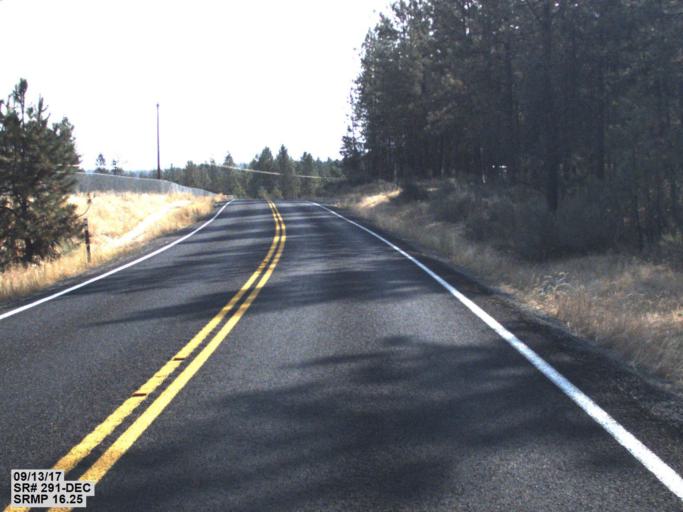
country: US
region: Washington
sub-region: Spokane County
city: Deer Park
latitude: 47.8403
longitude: -117.6126
